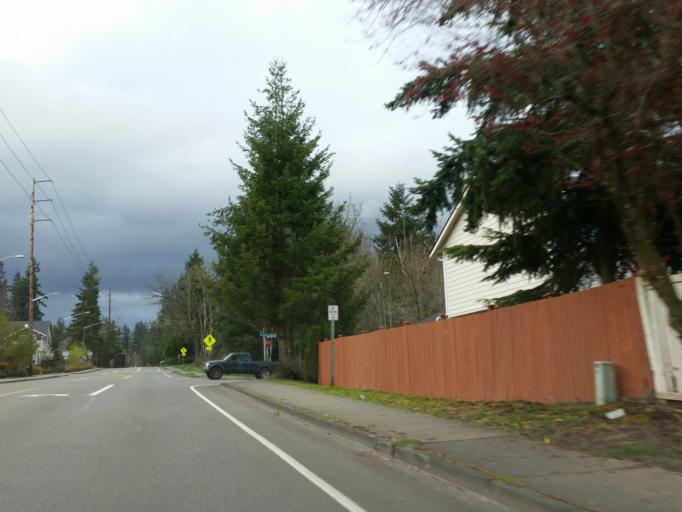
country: US
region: Washington
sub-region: King County
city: Woodinville
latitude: 47.7710
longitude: -122.1666
